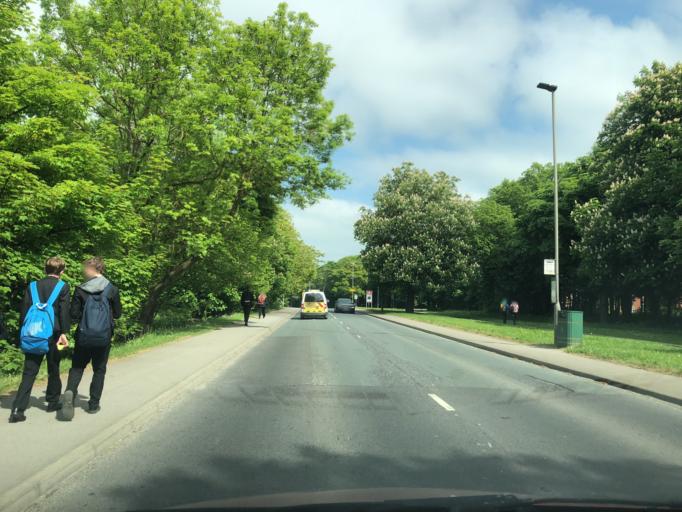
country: GB
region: England
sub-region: North Yorkshire
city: Catterick Garrison
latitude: 54.3764
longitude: -1.6998
